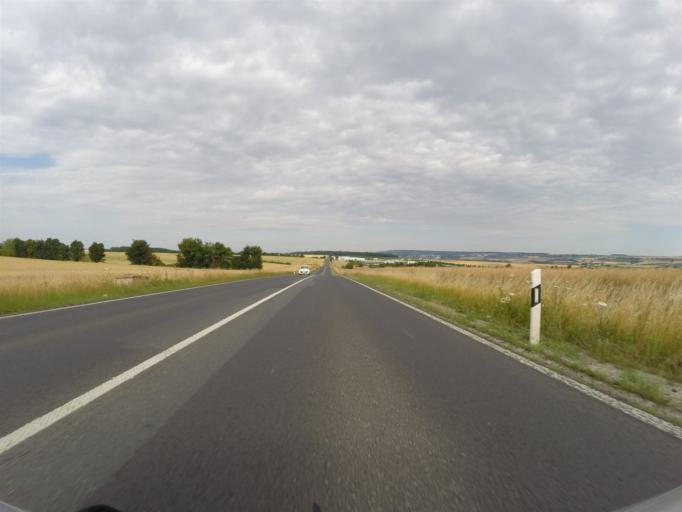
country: DE
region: Thuringia
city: Umpferstedt
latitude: 50.9788
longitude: 11.3960
